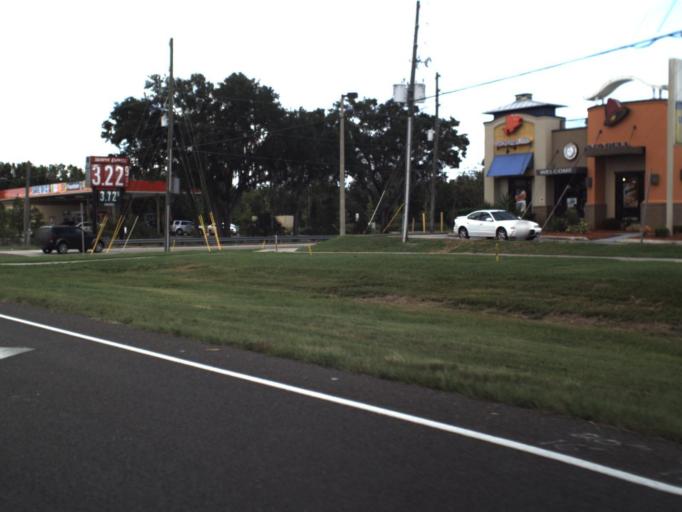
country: US
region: Florida
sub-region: Polk County
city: Medulla
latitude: 27.9342
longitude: -81.9739
